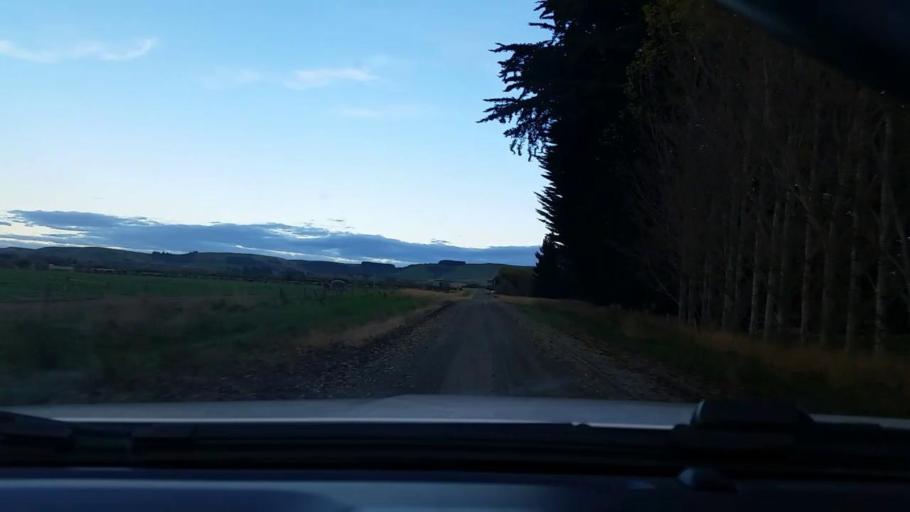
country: NZ
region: Southland
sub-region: Southland District
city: Winton
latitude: -46.1059
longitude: 168.4519
